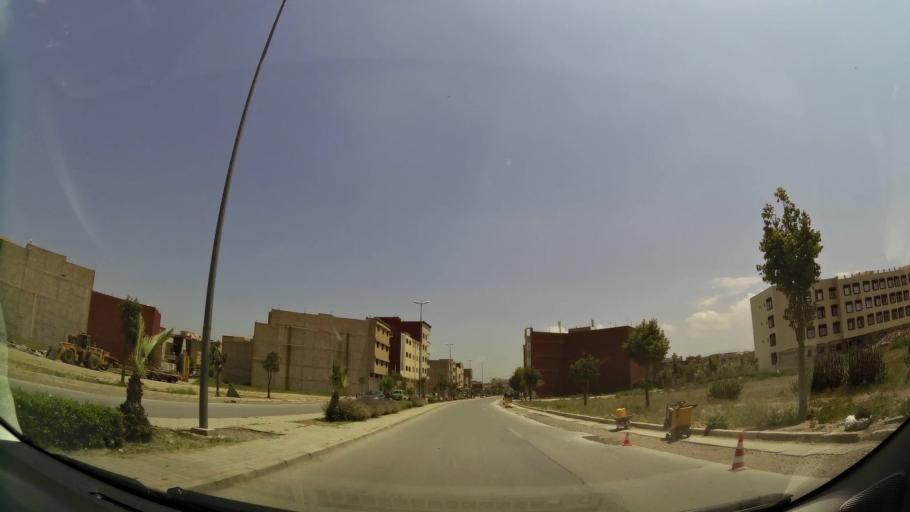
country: MA
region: Oriental
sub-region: Oujda-Angad
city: Oujda
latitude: 34.6913
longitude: -1.8951
